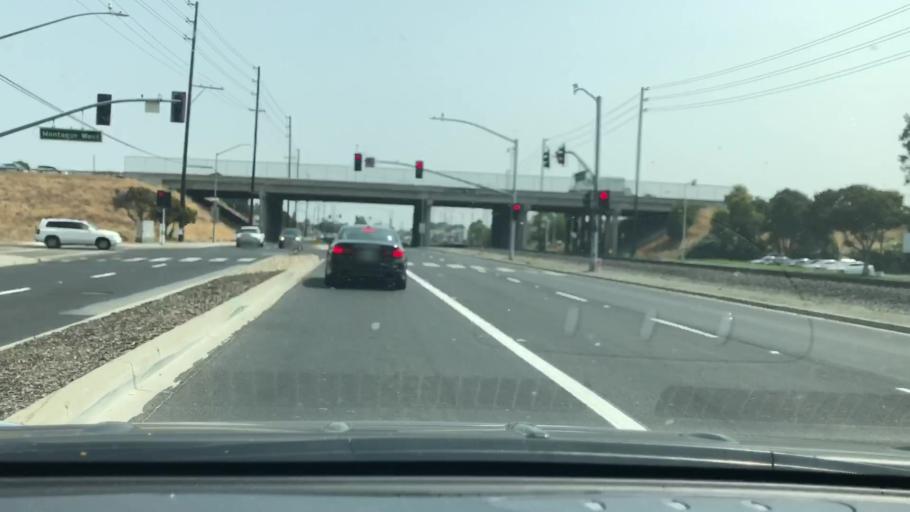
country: US
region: California
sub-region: Santa Clara County
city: Santa Clara
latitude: 37.3906
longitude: -121.9558
